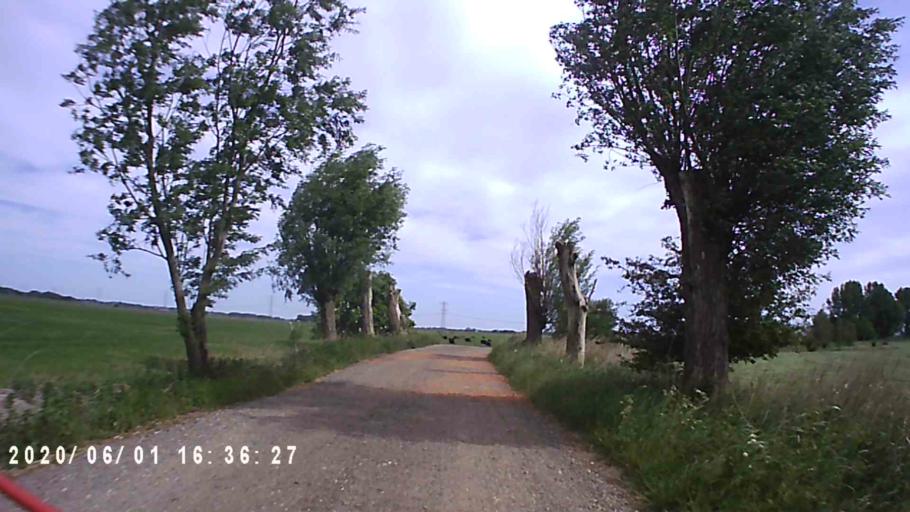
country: NL
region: Friesland
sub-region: Gemeente Tytsjerksteradiel
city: Tytsjerk
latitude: 53.1929
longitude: 5.8778
